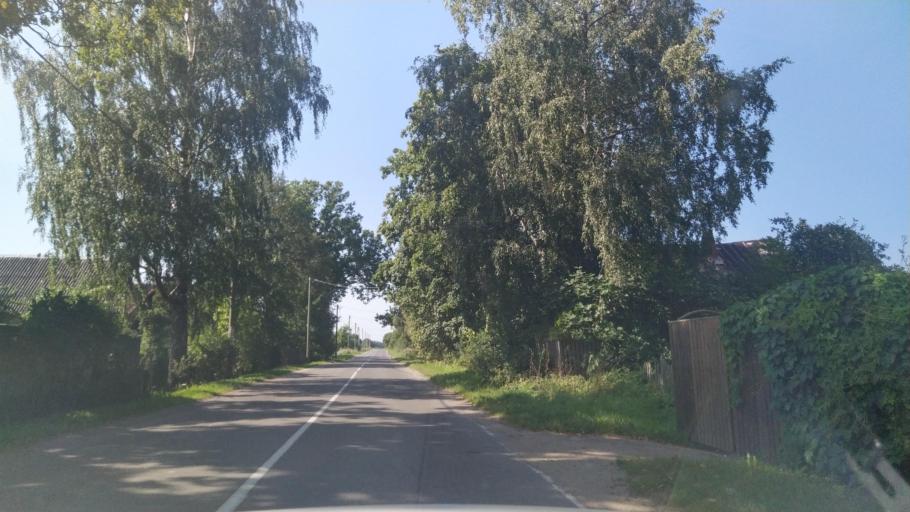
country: RU
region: Leningrad
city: Siverskiy
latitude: 59.2895
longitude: 30.0621
